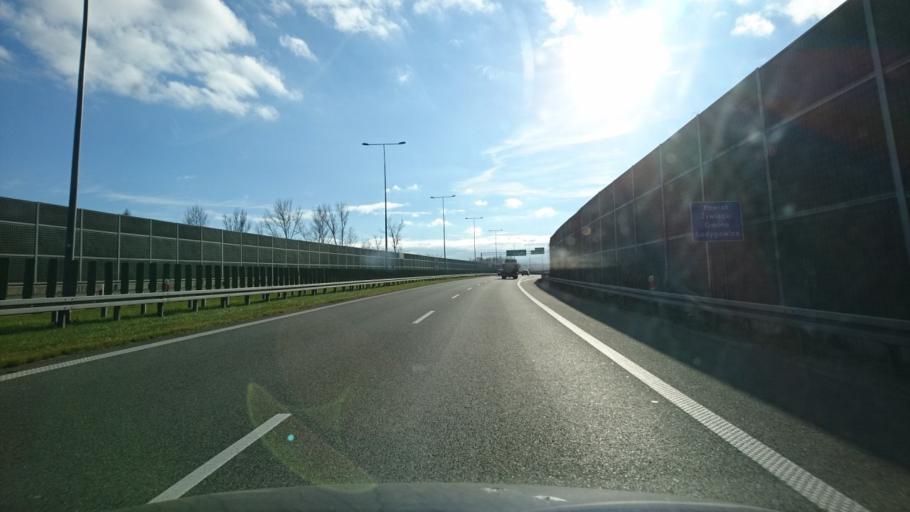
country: PL
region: Silesian Voivodeship
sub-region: Powiat zywiecki
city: Lodygowice
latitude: 49.7167
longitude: 19.1222
